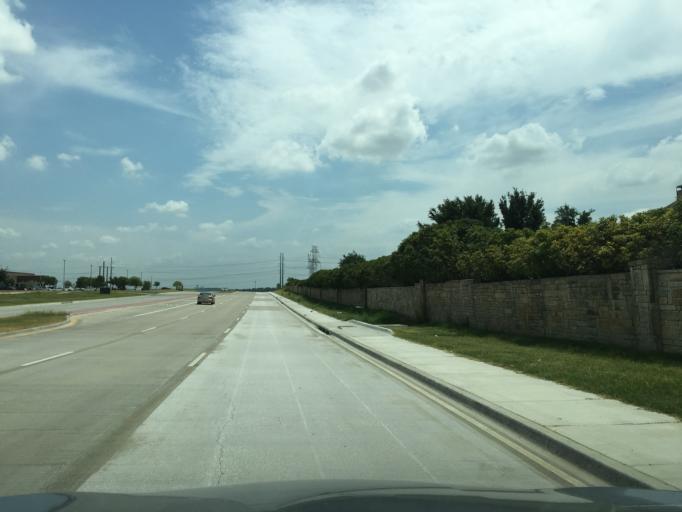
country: US
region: Texas
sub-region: Denton County
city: The Colony
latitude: 33.0462
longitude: -96.9102
